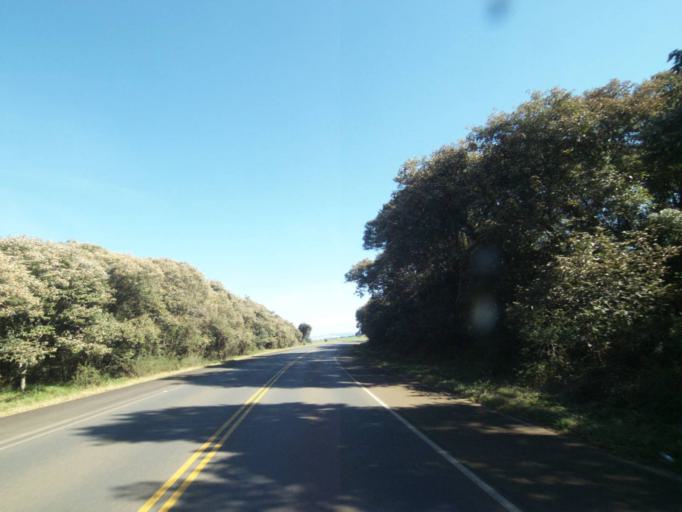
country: BR
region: Parana
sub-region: Tibagi
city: Tibagi
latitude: -24.4261
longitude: -50.3978
